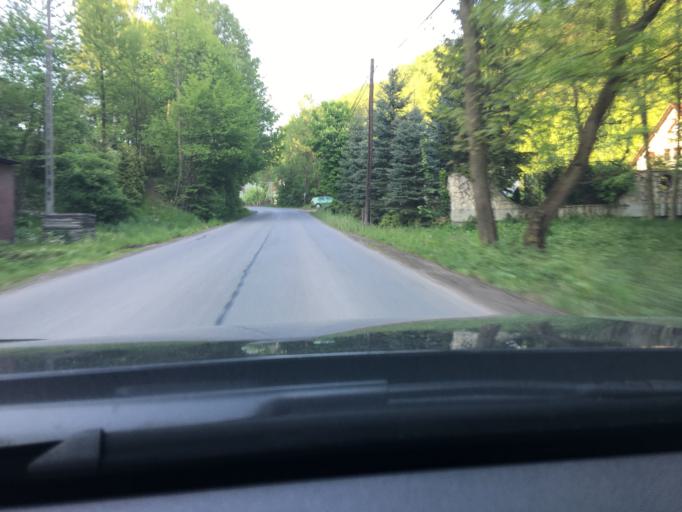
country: PL
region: Lesser Poland Voivodeship
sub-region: Powiat krakowski
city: Jerzmanowice
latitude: 50.1982
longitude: 19.7297
